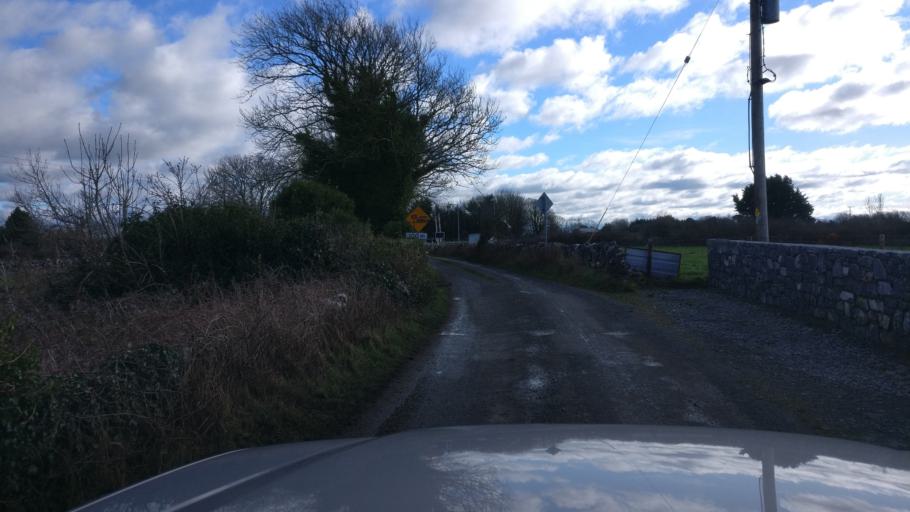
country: IE
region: Connaught
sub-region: County Galway
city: Oranmore
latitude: 53.2819
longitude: -8.8954
